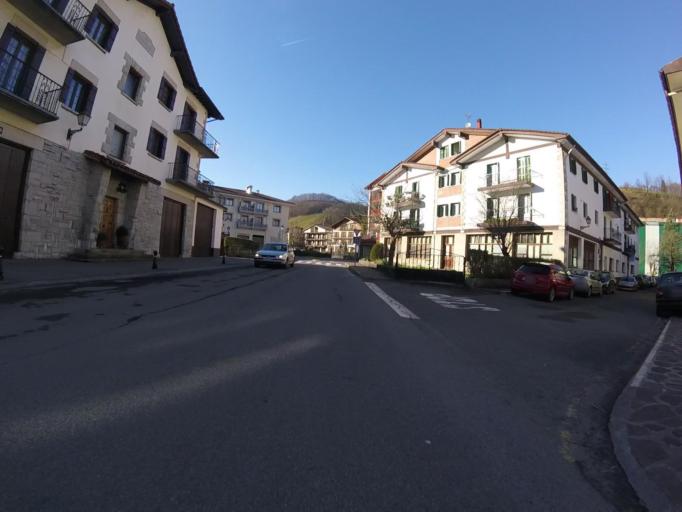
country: ES
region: Navarre
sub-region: Provincia de Navarra
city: Lesaka
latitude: 43.2471
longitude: -1.7083
